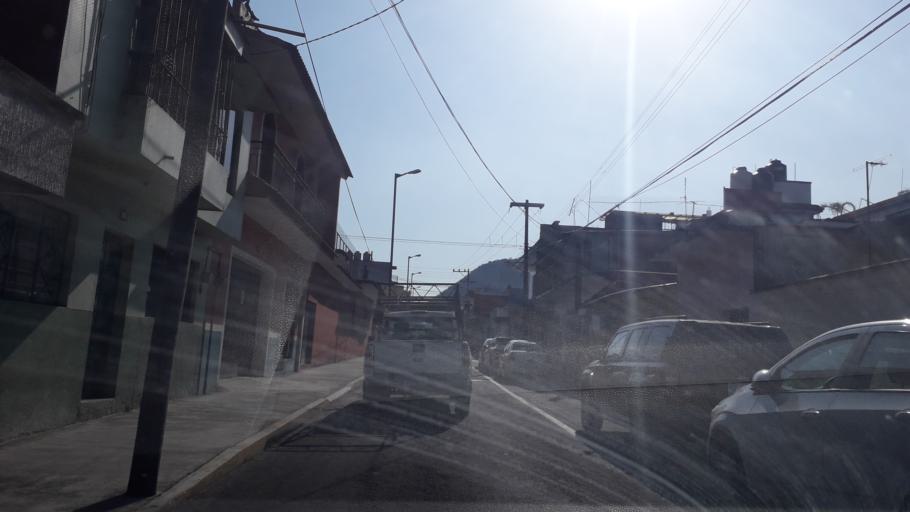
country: MX
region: Veracruz
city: Orizaba
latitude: 18.8462
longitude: -97.0970
